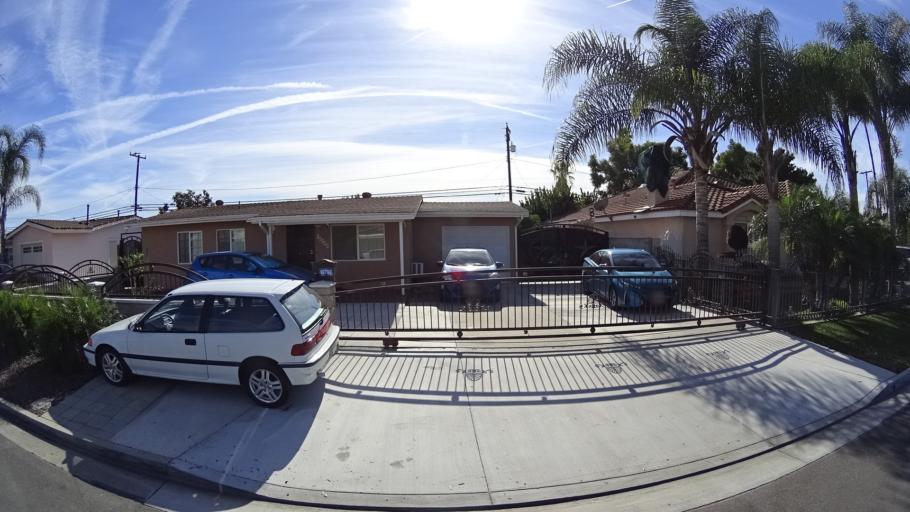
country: US
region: California
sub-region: Orange County
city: Garden Grove
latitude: 33.7636
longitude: -117.9411
